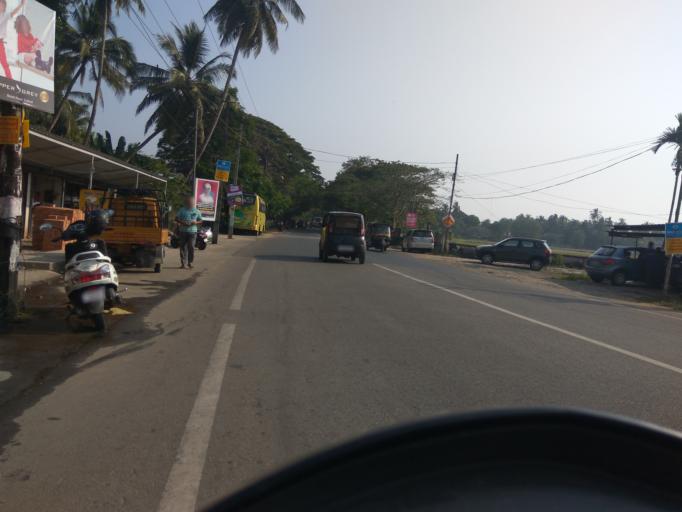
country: IN
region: Kerala
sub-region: Kozhikode
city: Kozhikode
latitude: 11.2881
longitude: 75.7670
